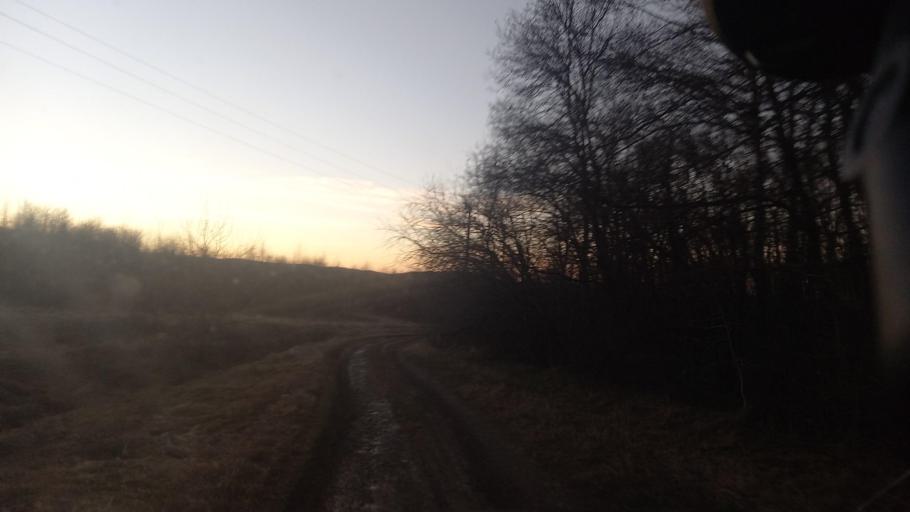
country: RU
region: Krasnodarskiy
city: Smolenskaya
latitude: 44.7271
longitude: 38.8397
